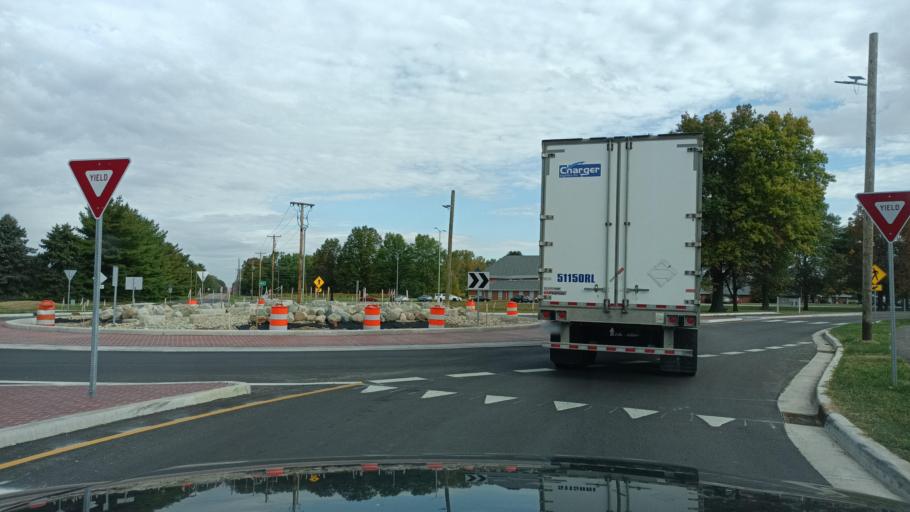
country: US
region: Indiana
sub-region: Delaware County
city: Yorktown
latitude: 40.1865
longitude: -85.4617
